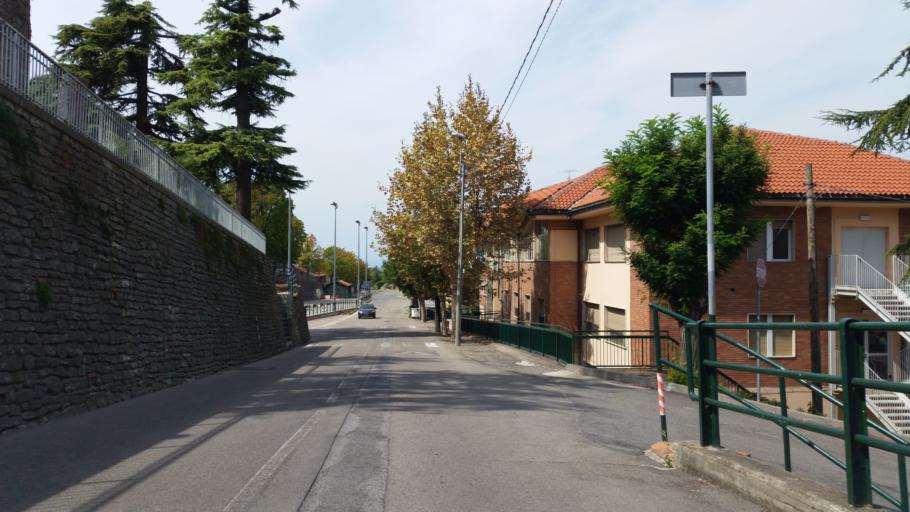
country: IT
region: Piedmont
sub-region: Provincia di Cuneo
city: Mango
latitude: 44.6858
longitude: 8.1498
